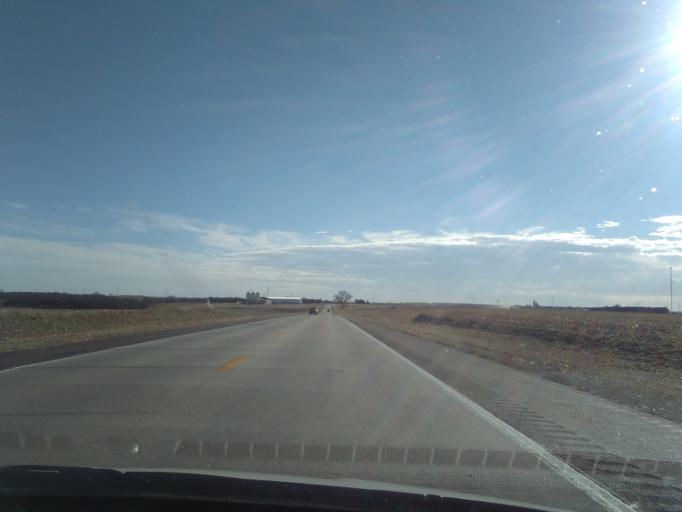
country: US
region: Nebraska
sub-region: Adams County
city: Hastings
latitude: 40.3632
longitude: -98.4397
